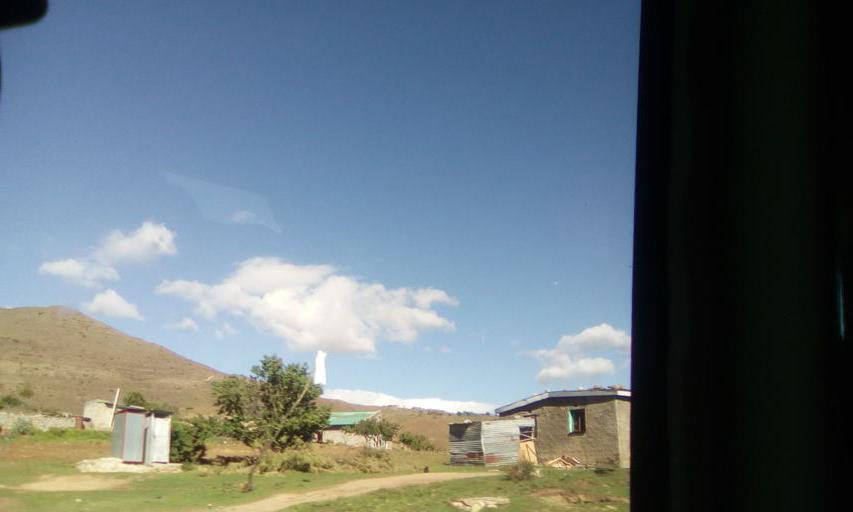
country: LS
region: Qacha's Nek
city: Qacha's Nek
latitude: -30.0580
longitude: 28.2891
